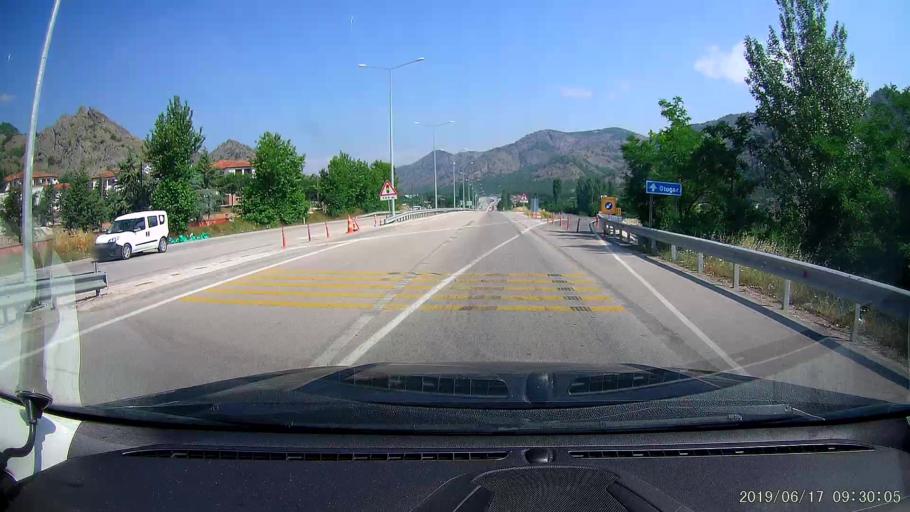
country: TR
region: Amasya
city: Amasya
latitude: 40.7021
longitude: 35.8057
